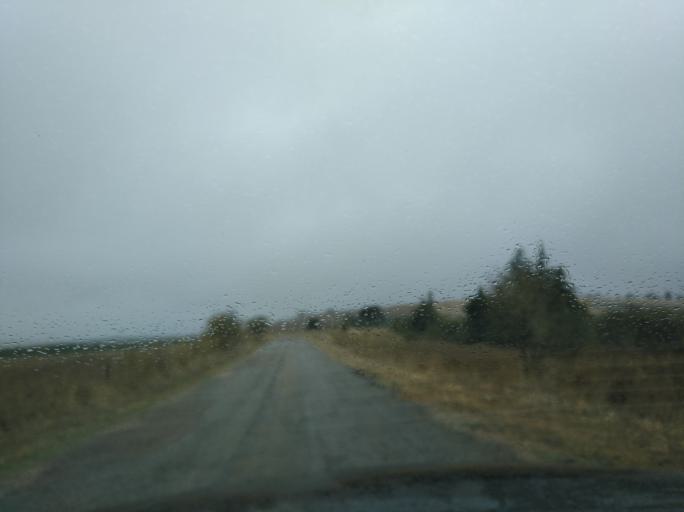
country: PT
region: Portalegre
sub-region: Campo Maior
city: Campo Maior
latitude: 38.9818
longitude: -7.0916
